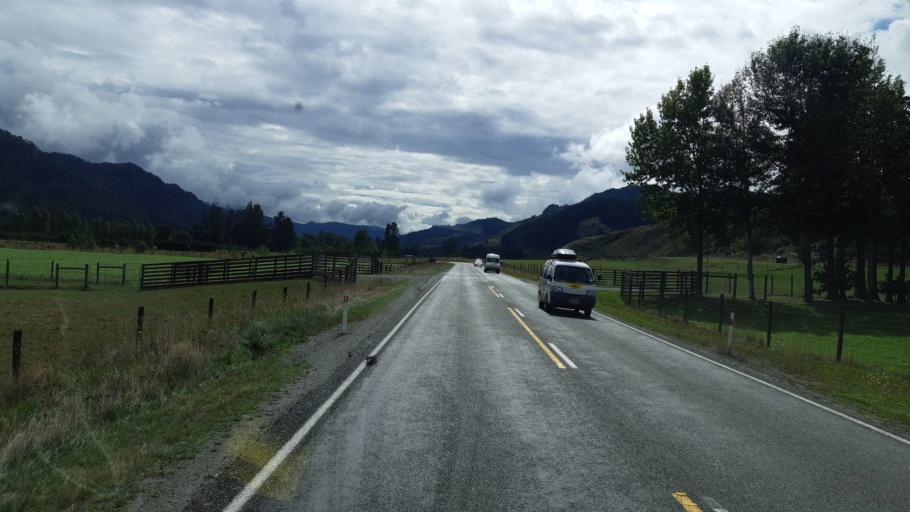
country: NZ
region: West Coast
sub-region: Buller District
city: Westport
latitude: -41.7795
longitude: 172.3751
